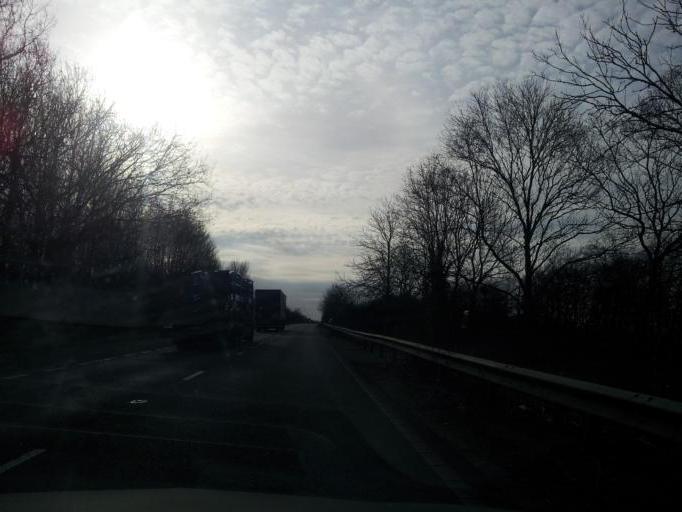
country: GB
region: England
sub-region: Peterborough
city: Castor
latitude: 52.5415
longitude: -0.3272
